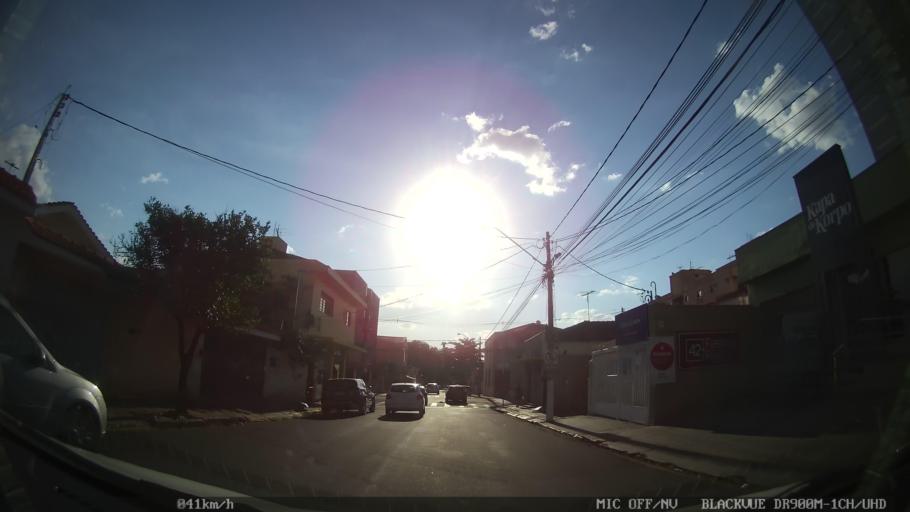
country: BR
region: Sao Paulo
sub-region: Ribeirao Preto
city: Ribeirao Preto
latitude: -21.1817
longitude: -47.7925
